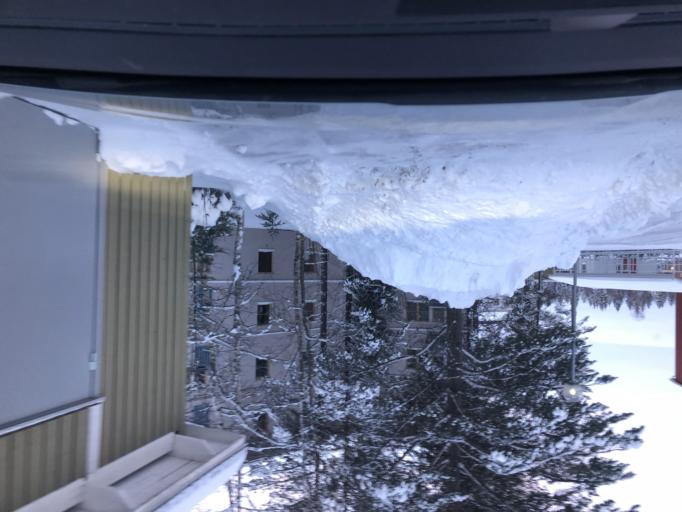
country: SE
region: Norrbotten
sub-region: Lulea Kommun
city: Bergnaset
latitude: 65.6228
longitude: 22.1184
